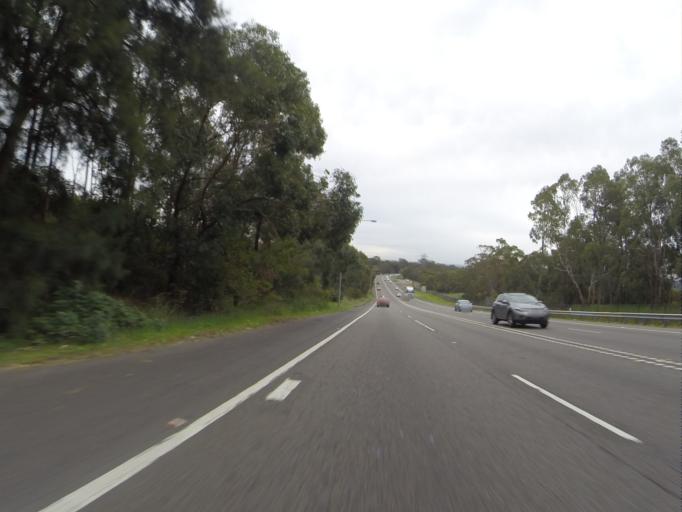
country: AU
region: New South Wales
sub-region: Hurstville
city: Lugarno
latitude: -33.9849
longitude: 151.0274
